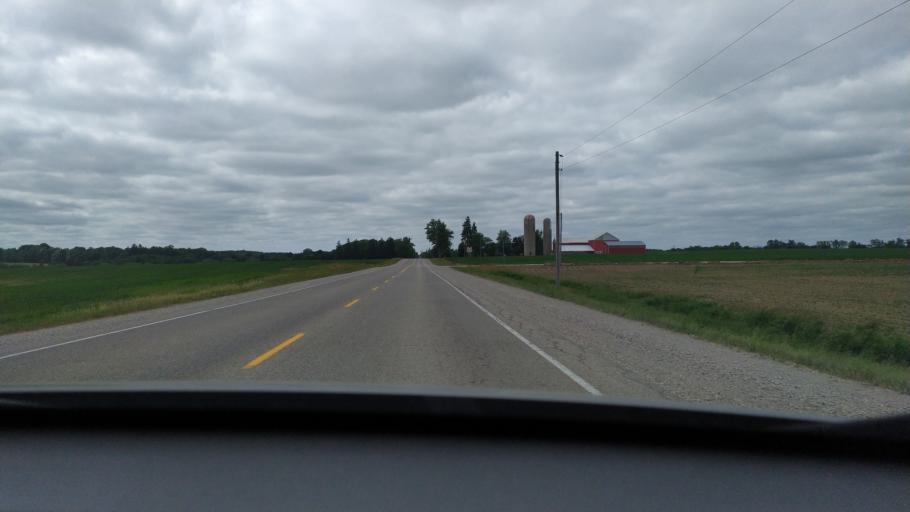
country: CA
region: Ontario
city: Stratford
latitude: 43.2873
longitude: -80.9683
